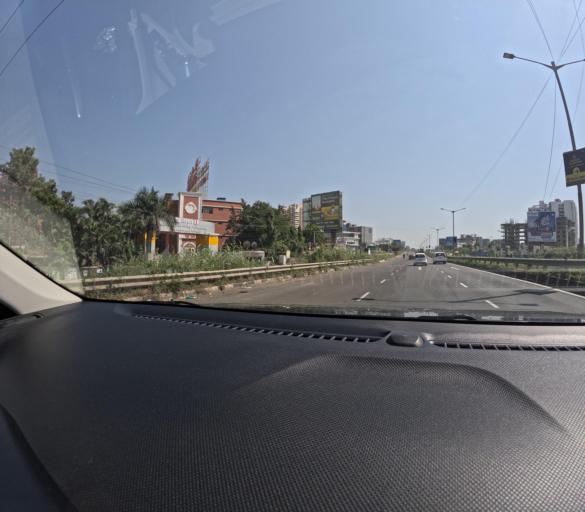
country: IN
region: Maharashtra
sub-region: Pune Division
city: Pimpri
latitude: 18.6207
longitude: 73.7463
